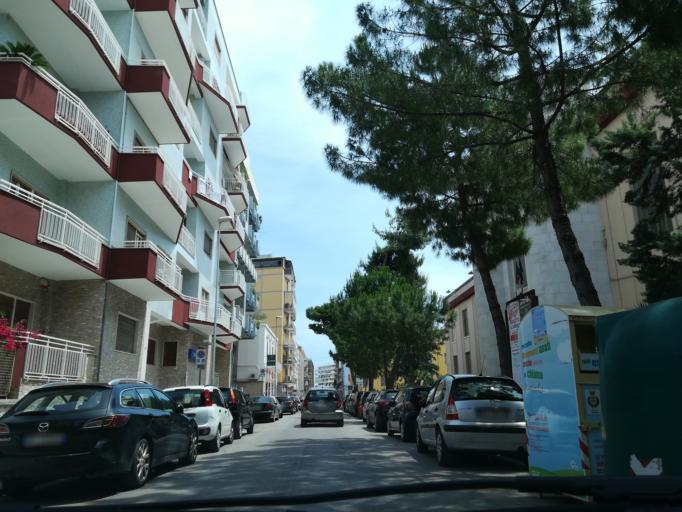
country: IT
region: Apulia
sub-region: Provincia di Barletta - Andria - Trani
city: Barletta
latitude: 41.3179
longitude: 16.2861
